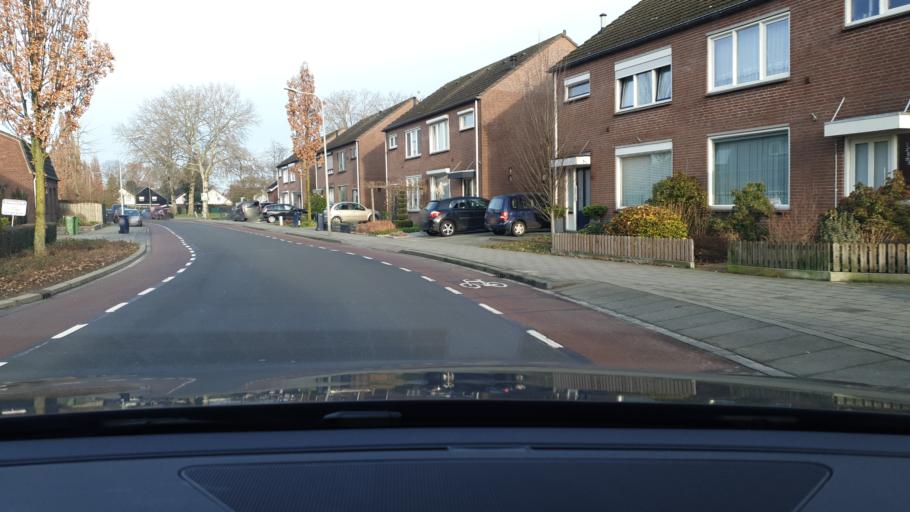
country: NL
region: Limburg
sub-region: Gemeente Peel en Maas
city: Maasbree
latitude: 51.4553
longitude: 6.0461
